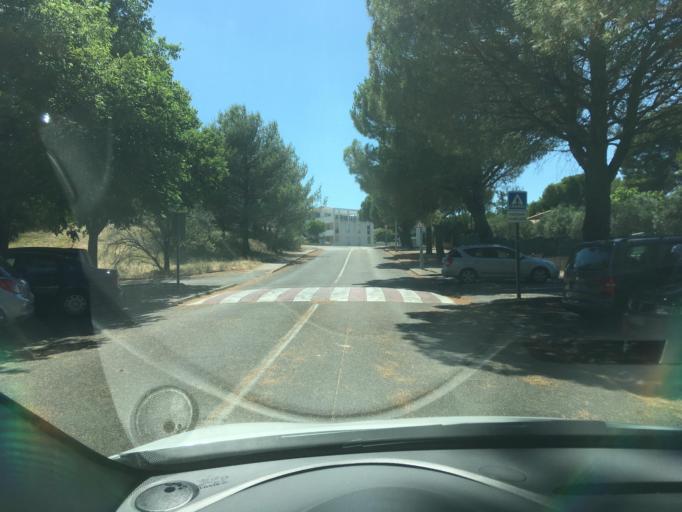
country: FR
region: Provence-Alpes-Cote d'Azur
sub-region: Departement des Bouches-du-Rhone
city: Chateaurenard
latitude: 43.8803
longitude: 4.8662
